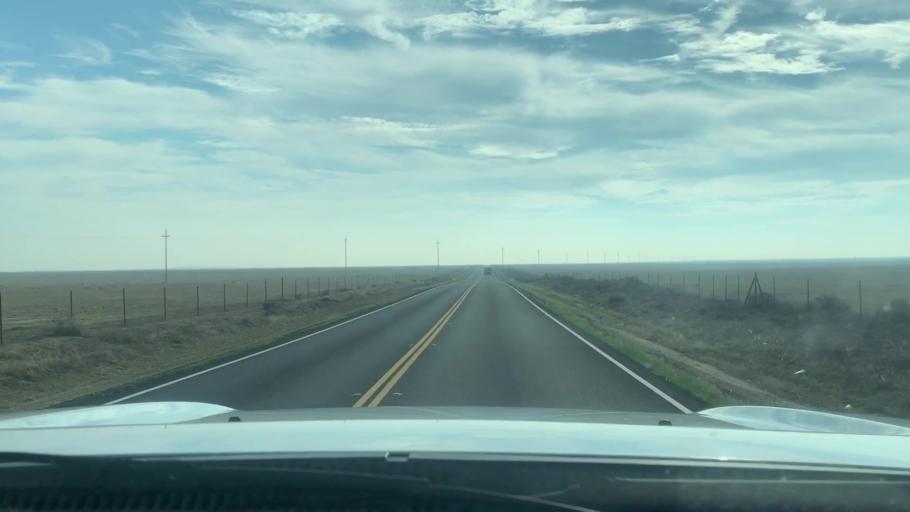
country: US
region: California
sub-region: Kern County
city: Lost Hills
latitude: 35.5932
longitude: -119.8410
